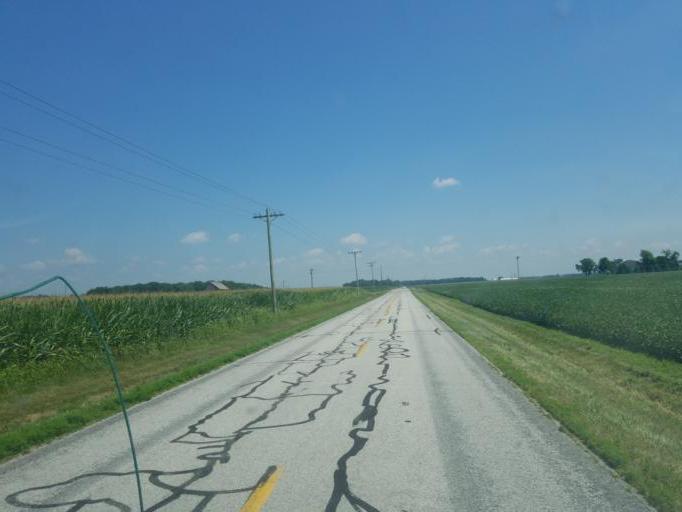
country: US
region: Ohio
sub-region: Auglaize County
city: Wapakoneta
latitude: 40.5404
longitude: -84.2617
